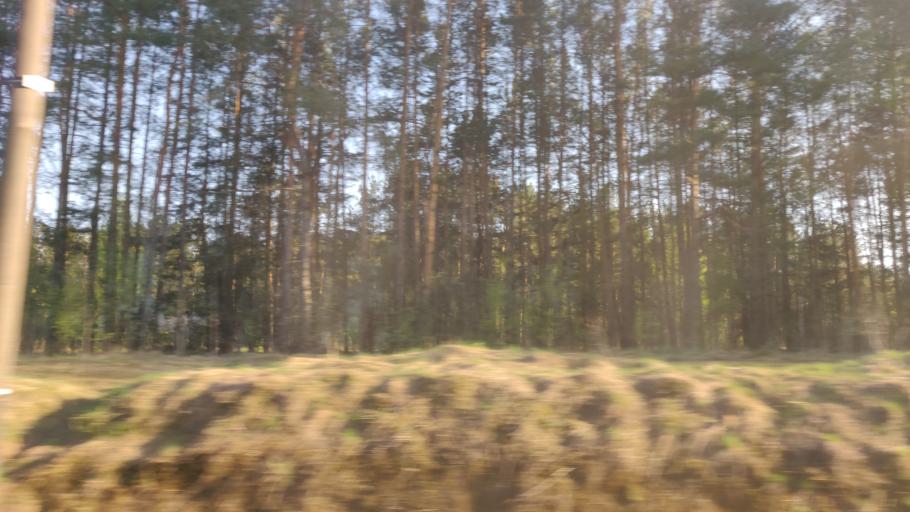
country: LT
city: Baltoji Voke
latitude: 54.6288
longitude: 25.1635
